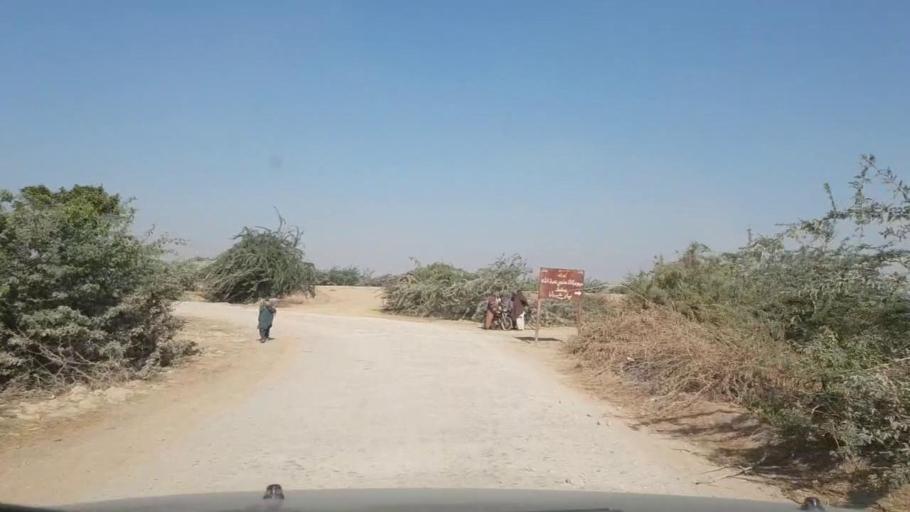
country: PK
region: Sindh
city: Thatta
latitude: 24.8020
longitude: 67.9021
